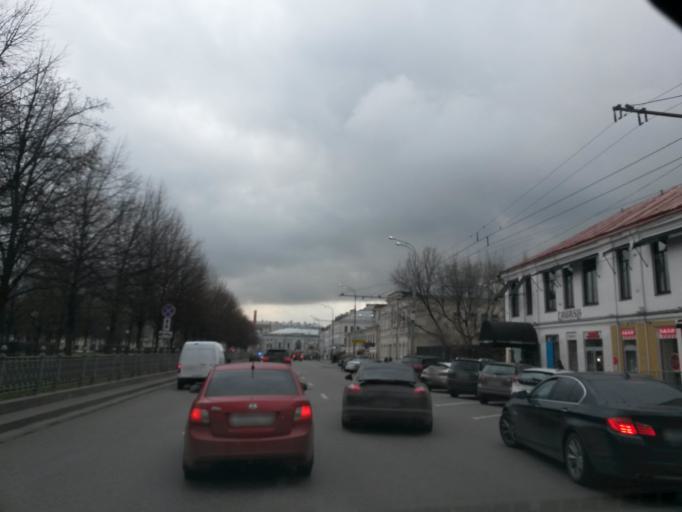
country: RU
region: Moscow
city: Moscow
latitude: 55.7696
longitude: 37.6211
